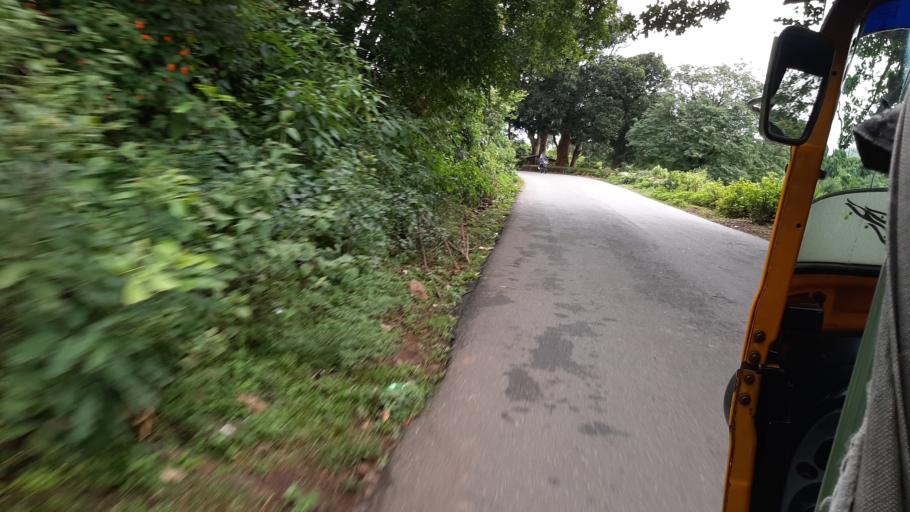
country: IN
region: Andhra Pradesh
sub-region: Vizianagaram District
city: Salur
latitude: 18.2454
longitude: 83.0253
